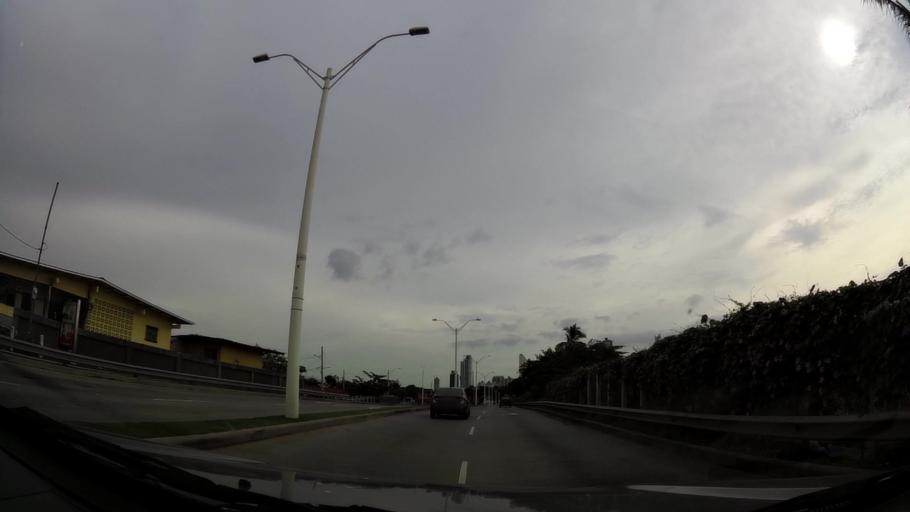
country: PA
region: Panama
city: Panama
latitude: 9.0064
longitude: -79.4905
